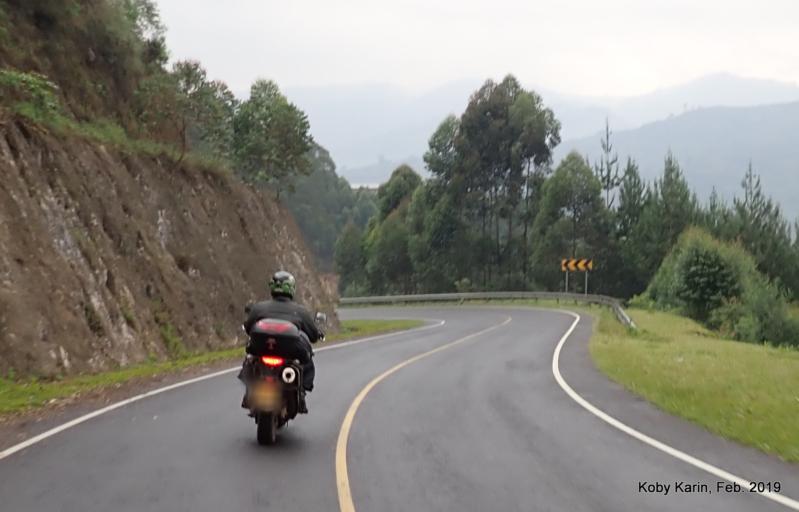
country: UG
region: Western Region
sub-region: Kabale District
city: Kabale
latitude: -1.1949
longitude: 29.8363
